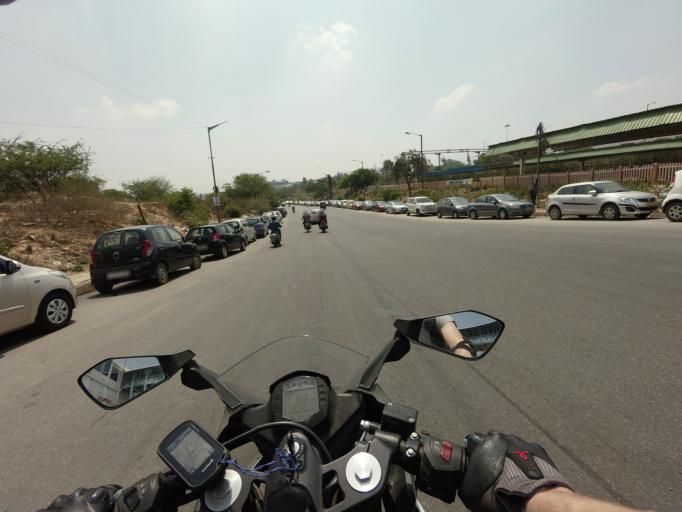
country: IN
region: Karnataka
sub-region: Bangalore Urban
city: Bangalore
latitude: 12.9916
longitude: 77.6528
